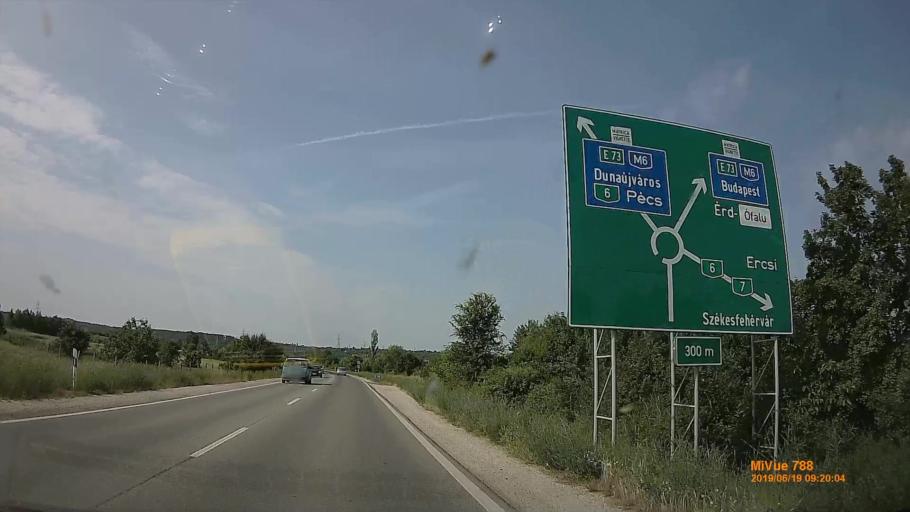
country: HU
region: Pest
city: Erd
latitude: 47.3751
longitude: 18.9341
